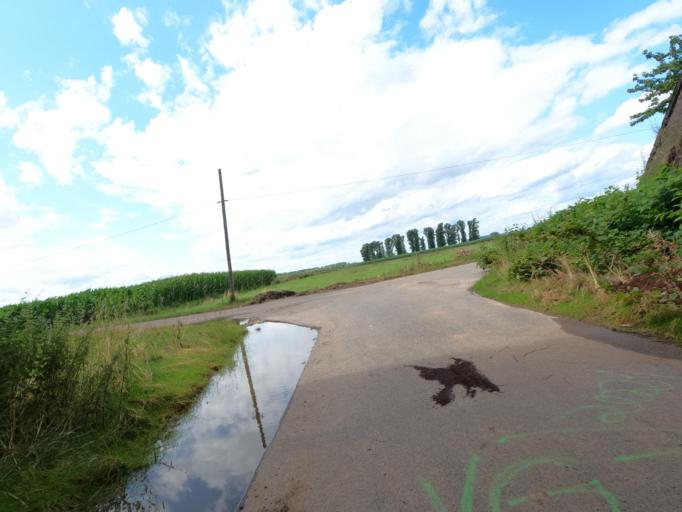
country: DE
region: North Rhine-Westphalia
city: Huckelhoven
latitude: 51.0153
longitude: 6.2429
